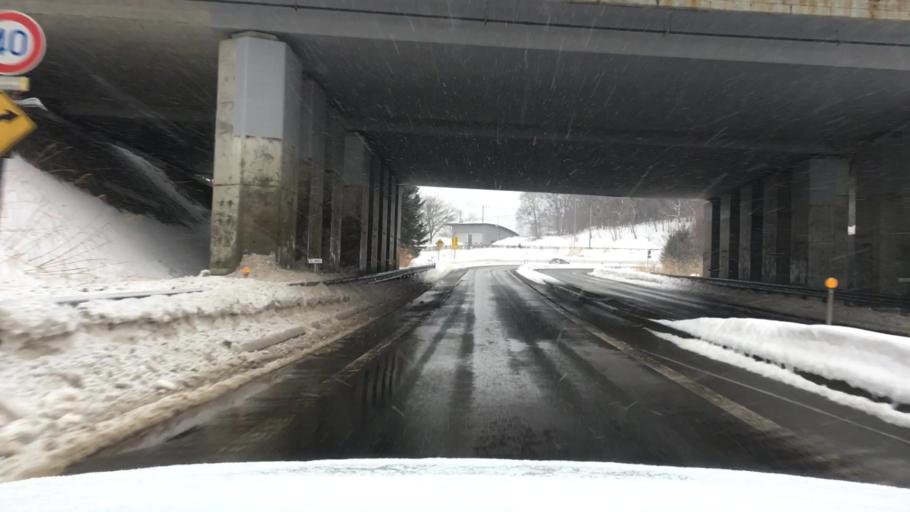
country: JP
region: Iwate
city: Ichinohe
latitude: 40.1096
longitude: 141.0486
